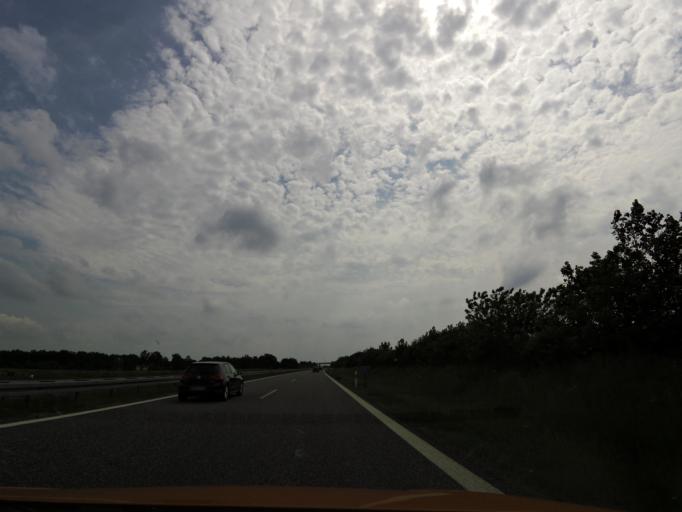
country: DE
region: Mecklenburg-Vorpommern
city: Mirow
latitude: 53.4723
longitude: 11.4916
